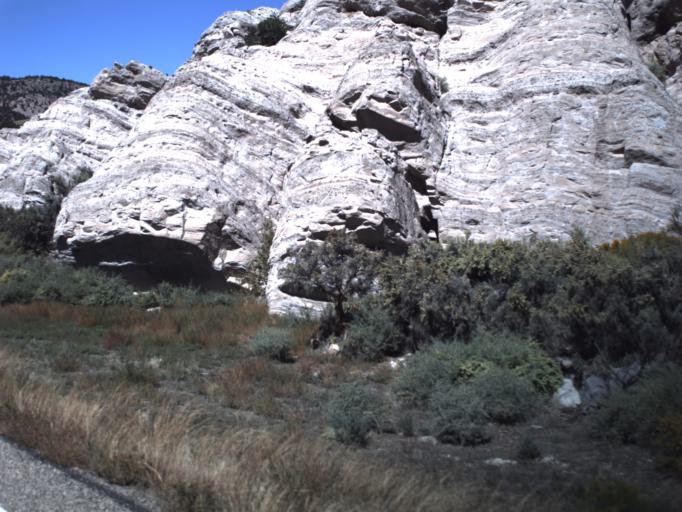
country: US
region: Utah
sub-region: Piute County
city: Junction
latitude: 38.1882
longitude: -112.0913
